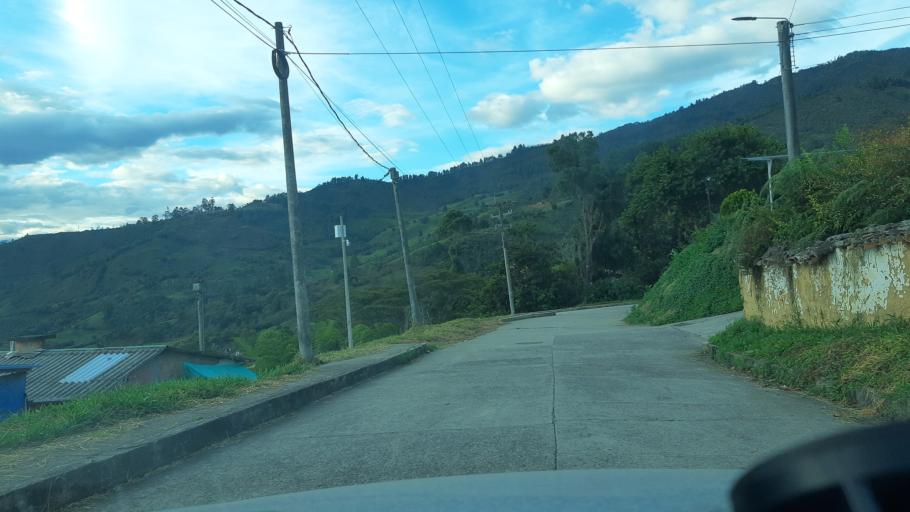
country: CO
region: Boyaca
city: Chivor
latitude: 4.9712
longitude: -73.3226
